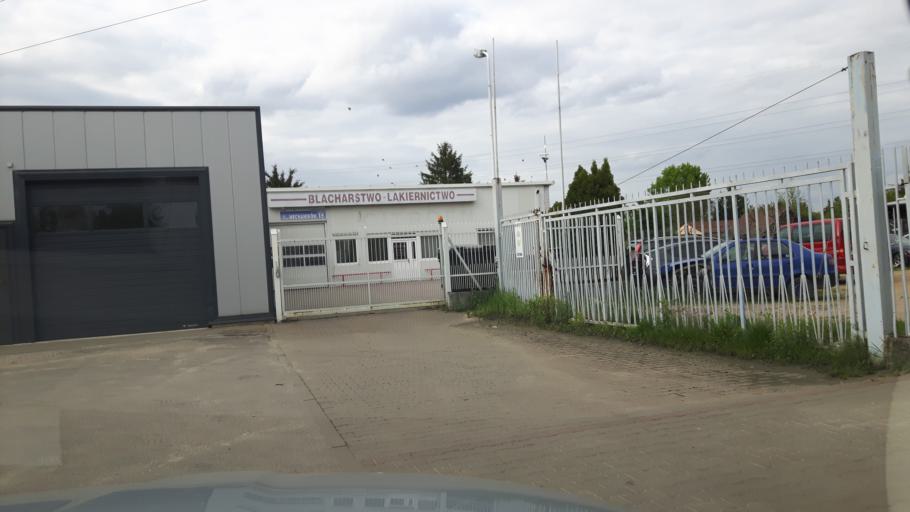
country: PL
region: Masovian Voivodeship
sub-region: Powiat wolominski
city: Zabki
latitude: 52.2888
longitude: 21.0889
